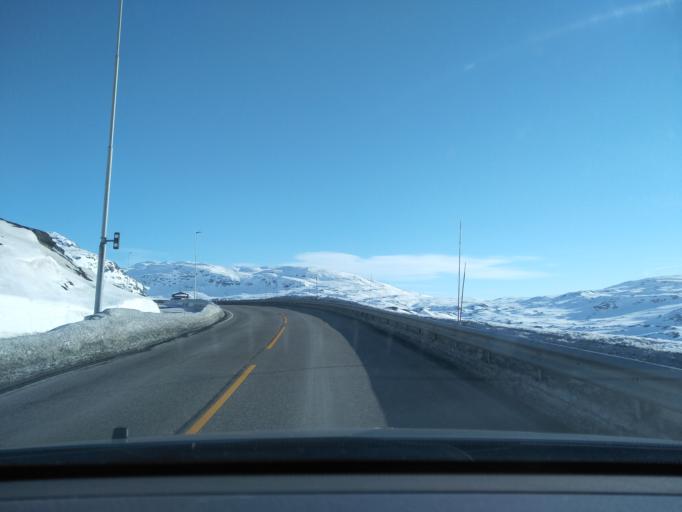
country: NO
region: Aust-Agder
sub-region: Bykle
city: Hovden
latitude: 59.8428
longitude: 6.9753
